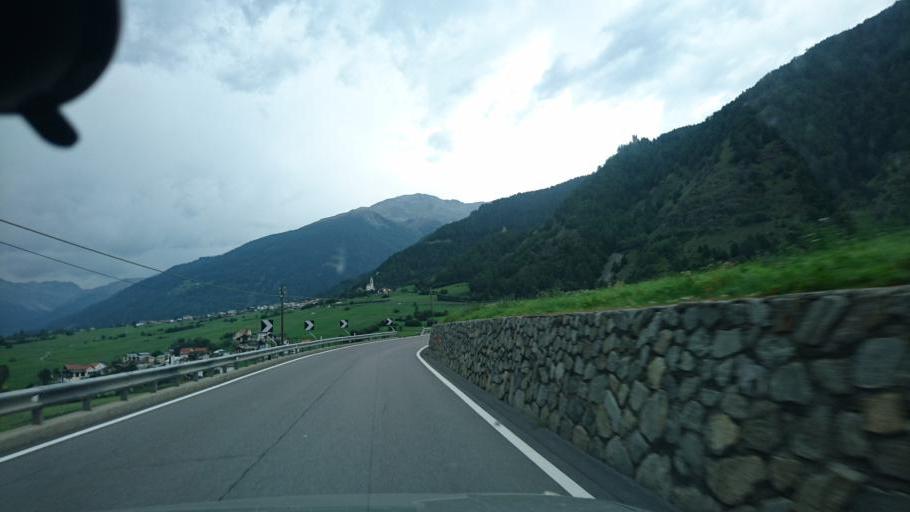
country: IT
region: Trentino-Alto Adige
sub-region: Bolzano
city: Tubre
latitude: 46.6539
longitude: 10.4842
